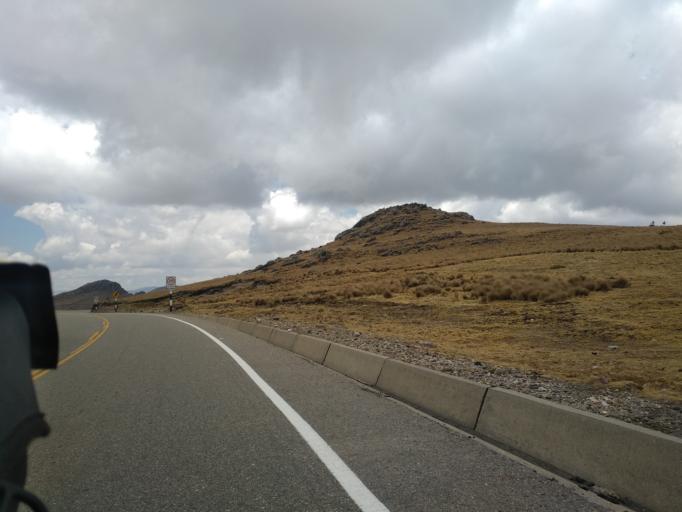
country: PE
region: La Libertad
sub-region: Provincia de Santiago de Chuco
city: Quiruvilca
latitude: -7.9691
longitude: -78.2048
